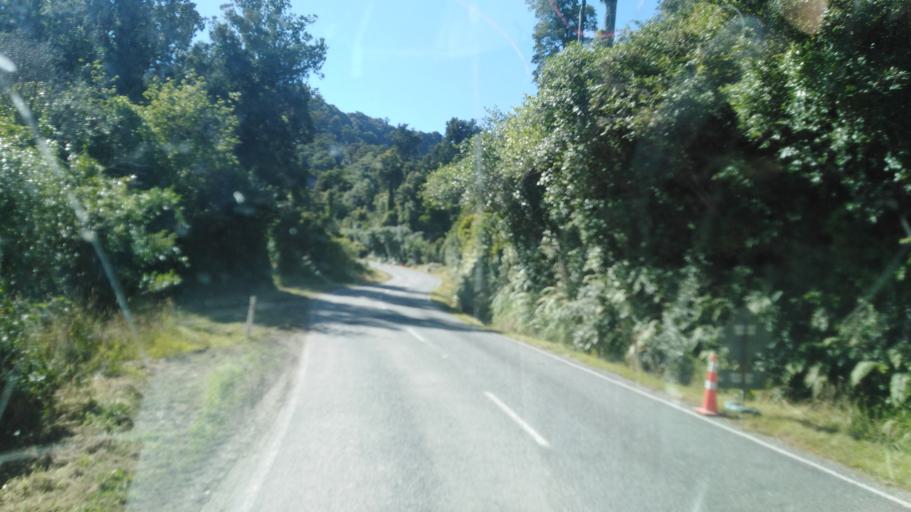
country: NZ
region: West Coast
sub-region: Buller District
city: Westport
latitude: -41.5291
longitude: 172.0048
